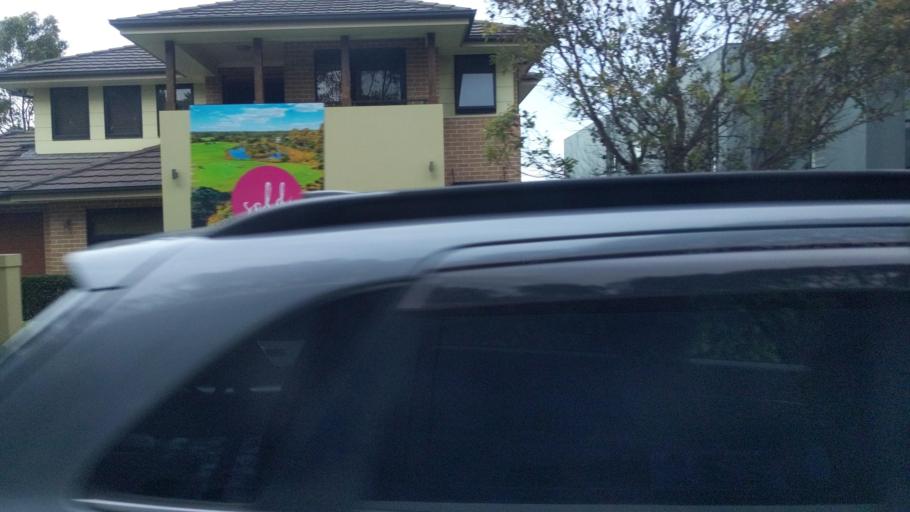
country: AU
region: New South Wales
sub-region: Blacktown
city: Quakers Hill
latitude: -33.7261
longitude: 150.8629
